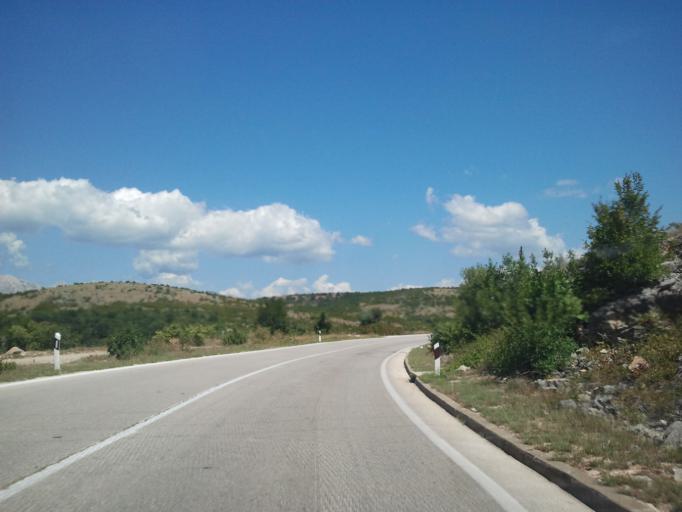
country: HR
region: Zadarska
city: Krusevo
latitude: 44.1797
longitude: 15.6171
